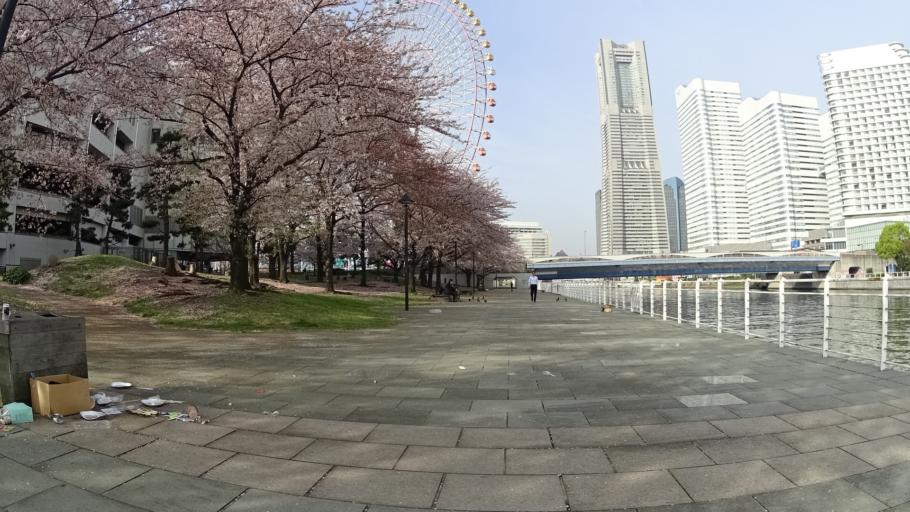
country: JP
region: Kanagawa
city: Yokohama
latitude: 35.4566
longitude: 139.6384
